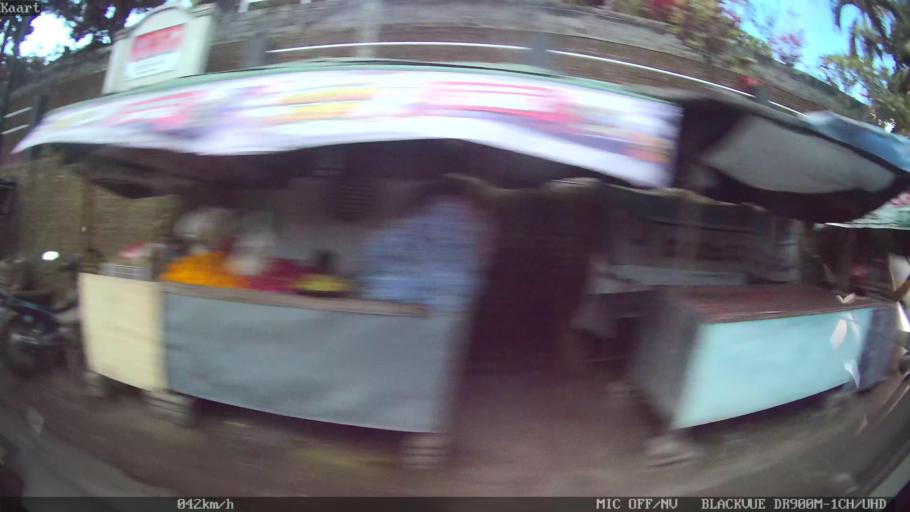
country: ID
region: Bali
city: Busungbiu
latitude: -8.2572
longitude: 114.9699
